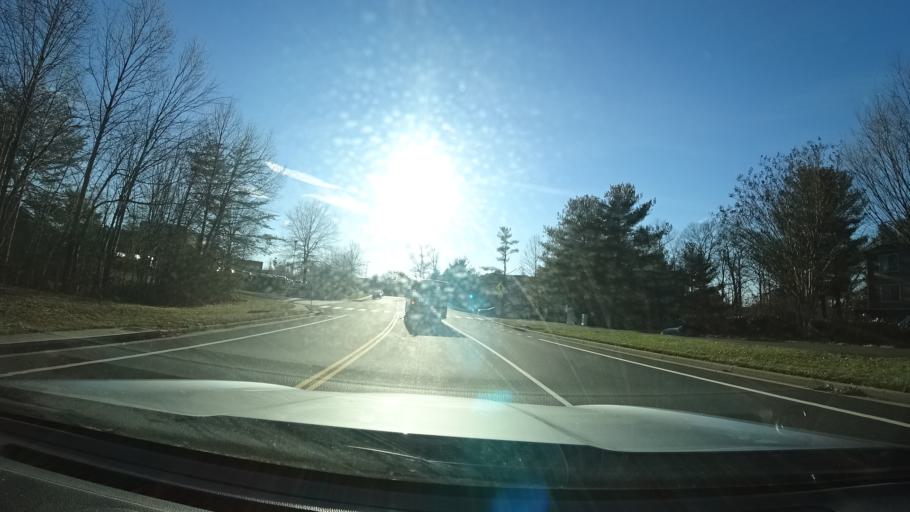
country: US
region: Virginia
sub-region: Fairfax County
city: Reston
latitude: 38.9682
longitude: -77.3588
